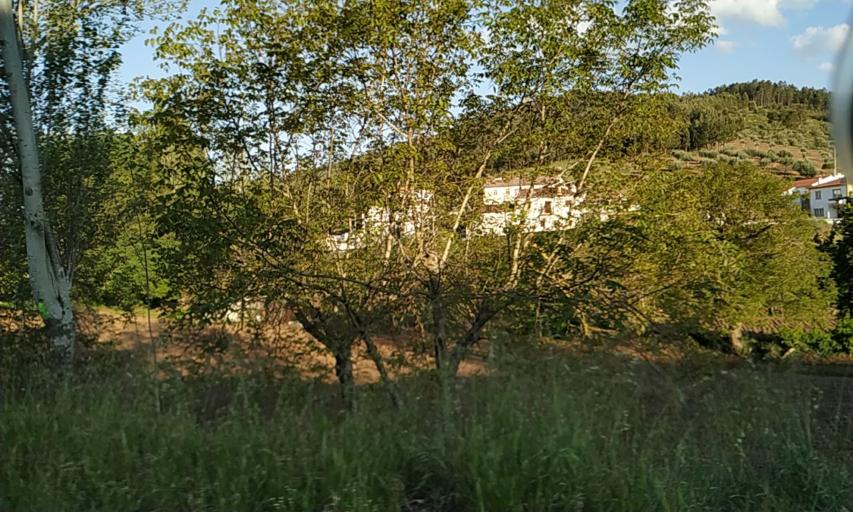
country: PT
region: Portalegre
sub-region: Marvao
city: Marvao
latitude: 39.3825
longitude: -7.3862
